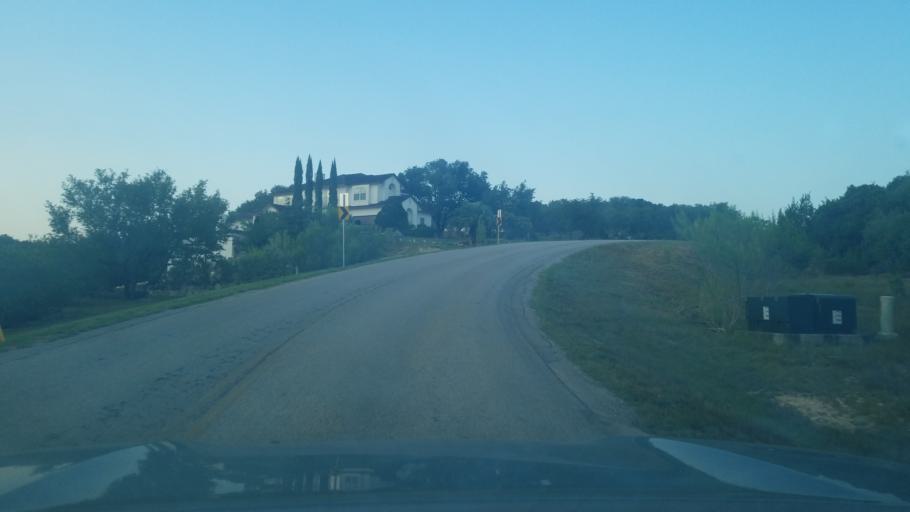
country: US
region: Texas
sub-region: Comal County
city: Bulverde
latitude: 29.8107
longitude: -98.4072
